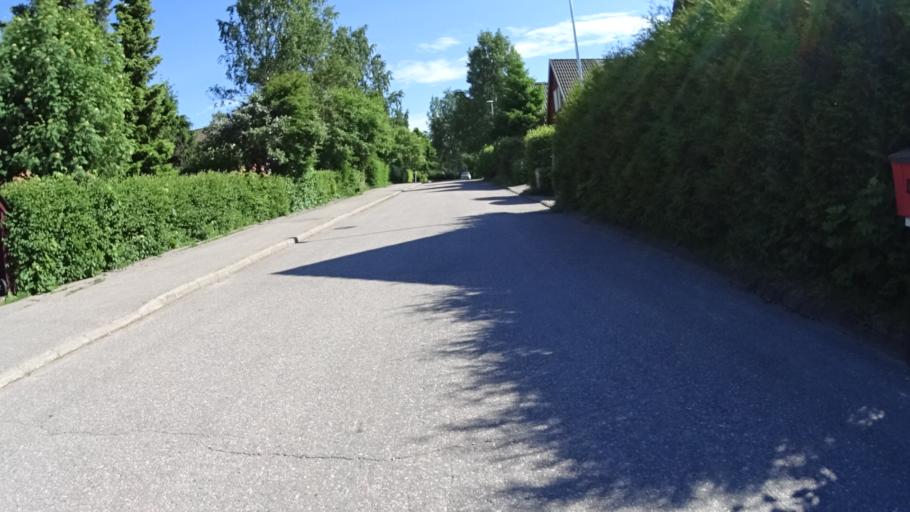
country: FI
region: Uusimaa
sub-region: Helsinki
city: Kilo
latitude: 60.2665
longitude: 24.7915
